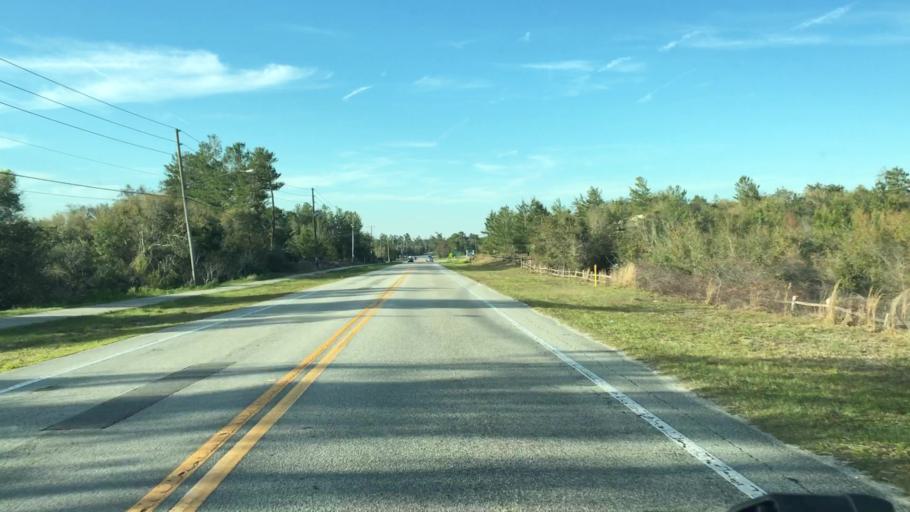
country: US
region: Florida
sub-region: Volusia County
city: Deltona
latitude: 28.9246
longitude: -81.2221
